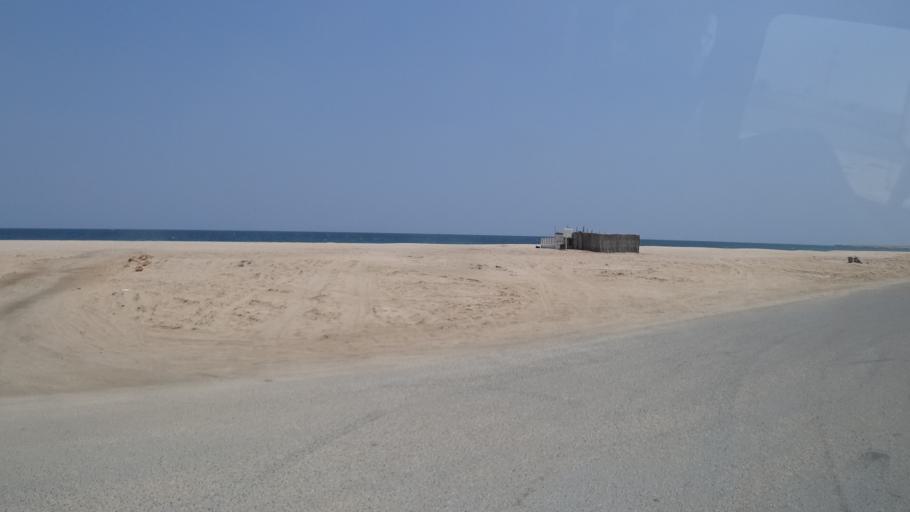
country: OM
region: Ash Sharqiyah
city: Sur
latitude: 22.5275
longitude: 59.7973
